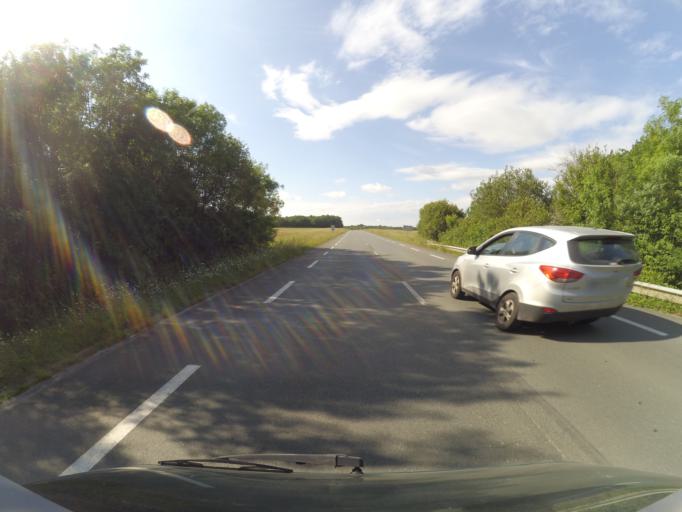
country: FR
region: Poitou-Charentes
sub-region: Departement de la Charente-Maritime
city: Saint-Agnant
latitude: 45.8300
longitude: -0.9368
